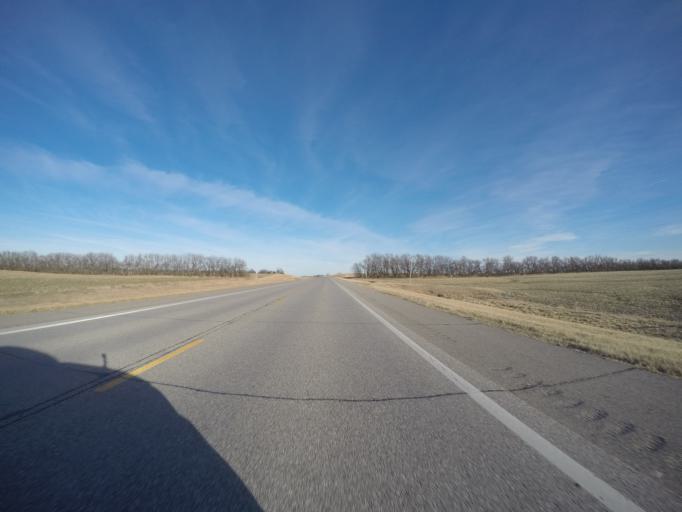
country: US
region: Kansas
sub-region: Marion County
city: Peabody
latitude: 38.1749
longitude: -97.1827
